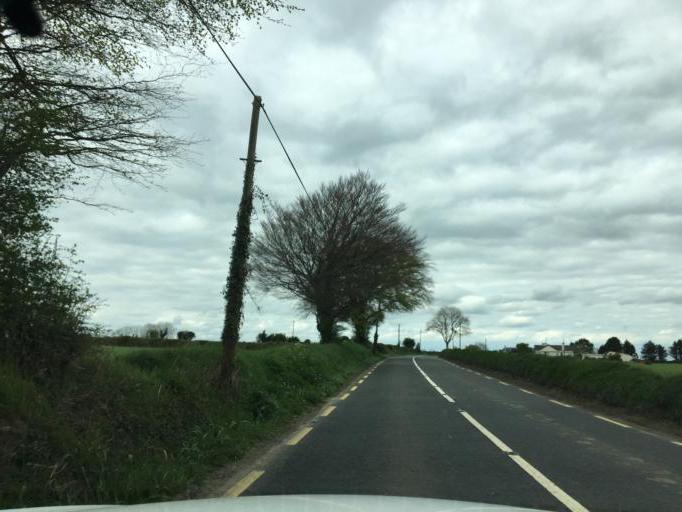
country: IE
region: Leinster
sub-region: Loch Garman
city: Enniscorthy
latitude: 52.4389
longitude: -6.7352
